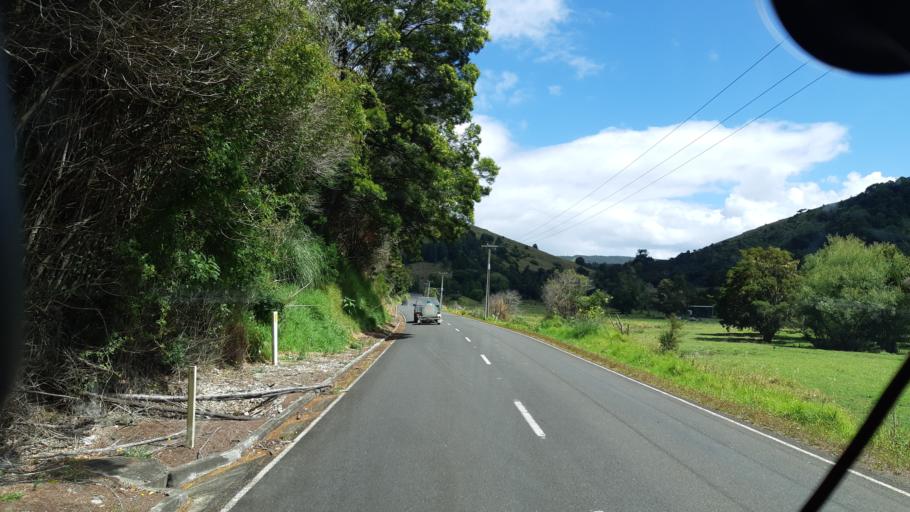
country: NZ
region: Northland
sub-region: Far North District
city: Taipa
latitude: -35.2704
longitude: 173.5060
